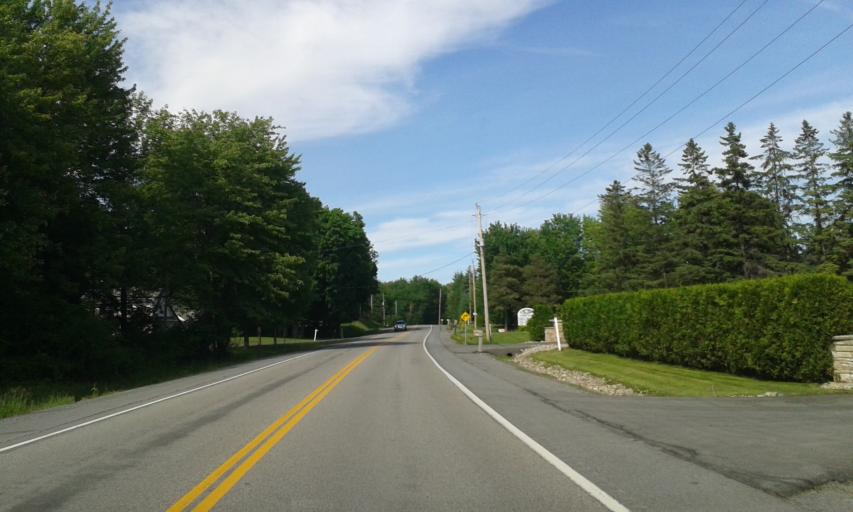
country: CA
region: Ontario
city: Cornwall
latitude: 45.1231
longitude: -74.5056
